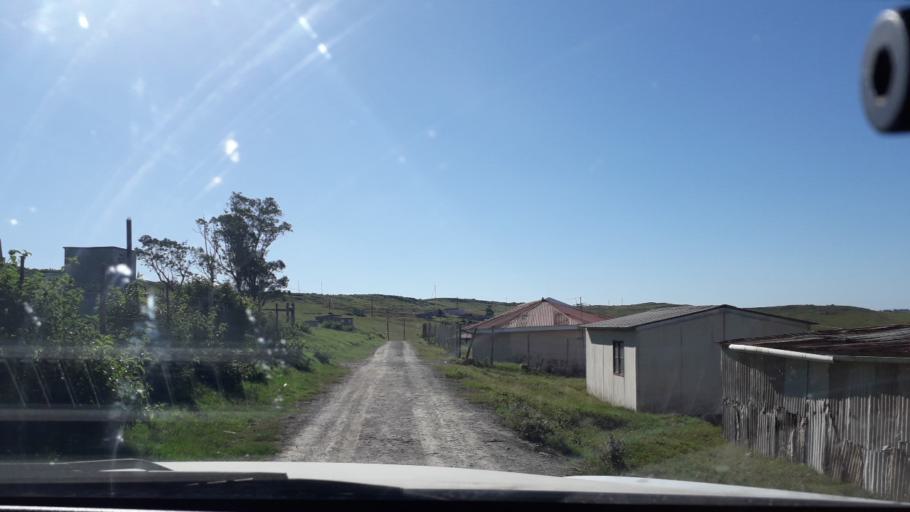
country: ZA
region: Eastern Cape
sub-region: Buffalo City Metropolitan Municipality
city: East London
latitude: -32.8425
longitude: 27.9925
